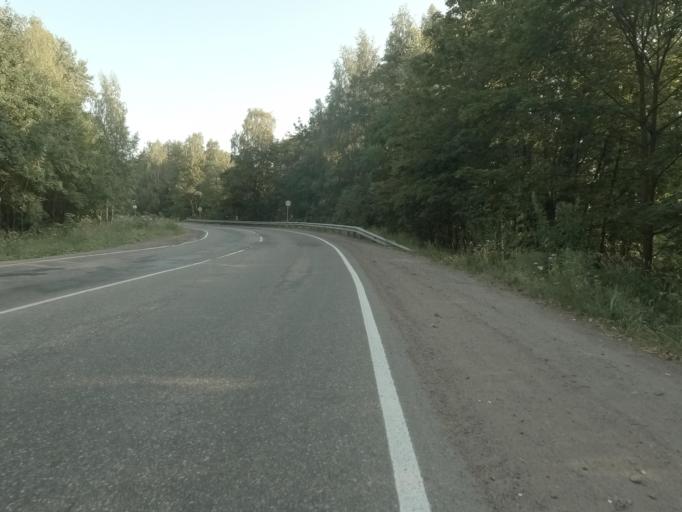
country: RU
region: Leningrad
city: Vyborg
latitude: 60.7285
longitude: 28.7597
